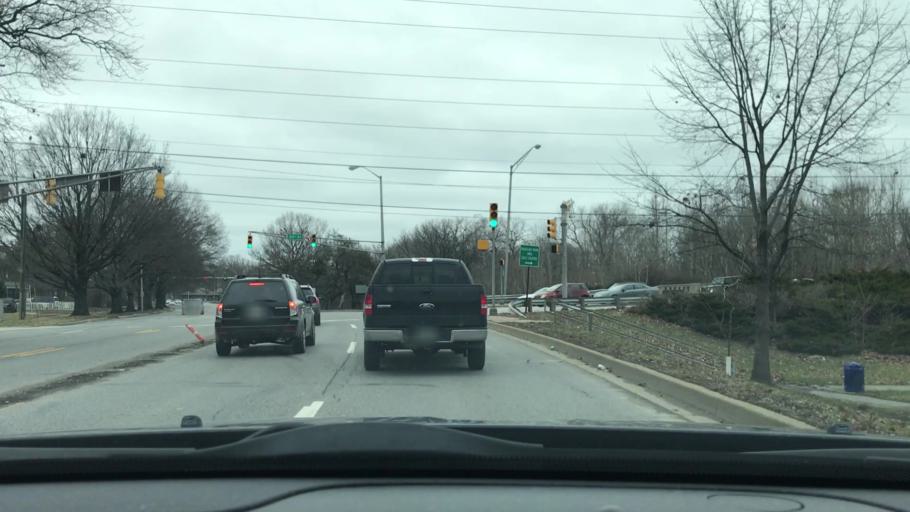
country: US
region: Indiana
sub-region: Marion County
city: Indianapolis
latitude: 39.8099
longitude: -86.1436
